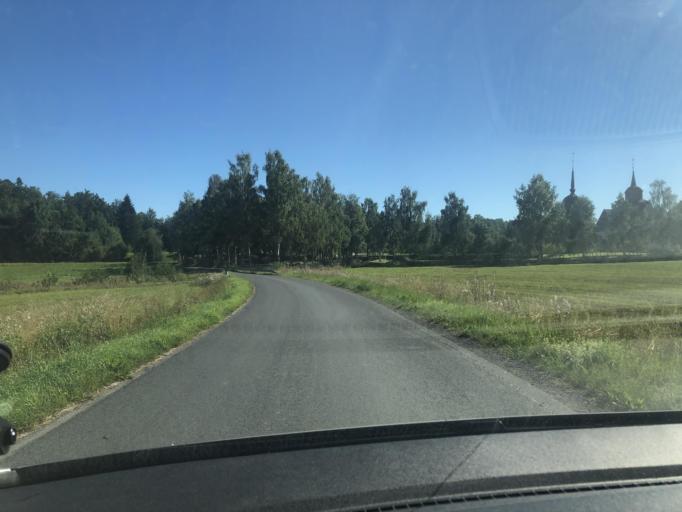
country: SE
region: Joenkoeping
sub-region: Jonkopings Kommun
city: Huskvarna
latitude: 57.7981
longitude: 14.3126
